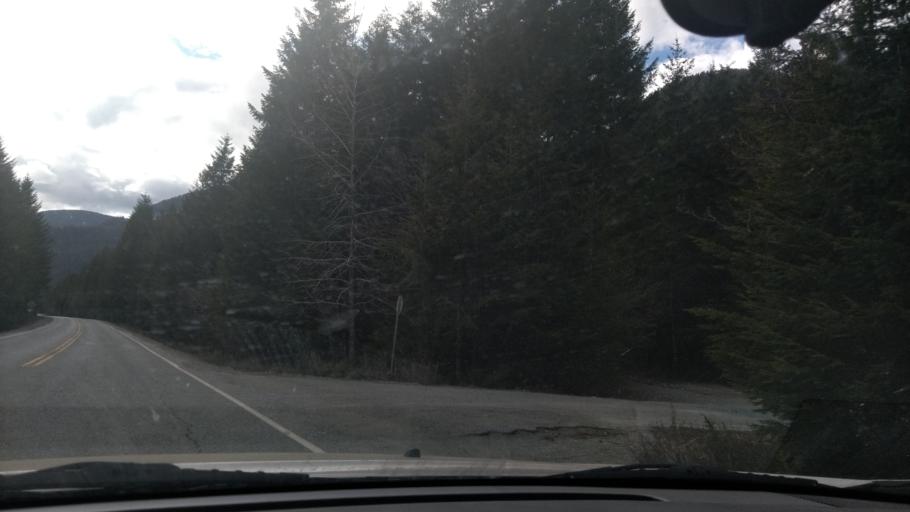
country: CA
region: British Columbia
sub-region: Regional District of Alberni-Clayoquot
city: Tofino
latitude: 49.8346
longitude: -125.9536
